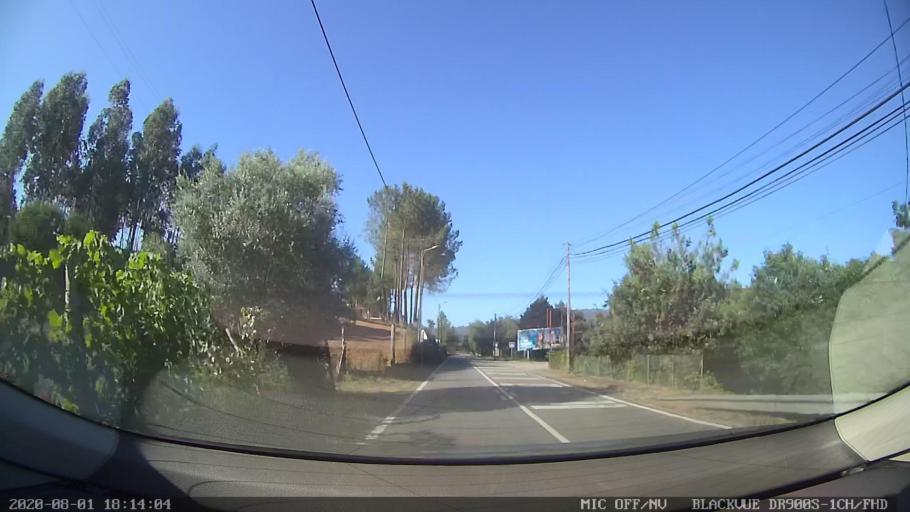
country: PT
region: Porto
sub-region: Pacos de Ferreira
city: Seroa
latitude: 41.2731
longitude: -8.4697
